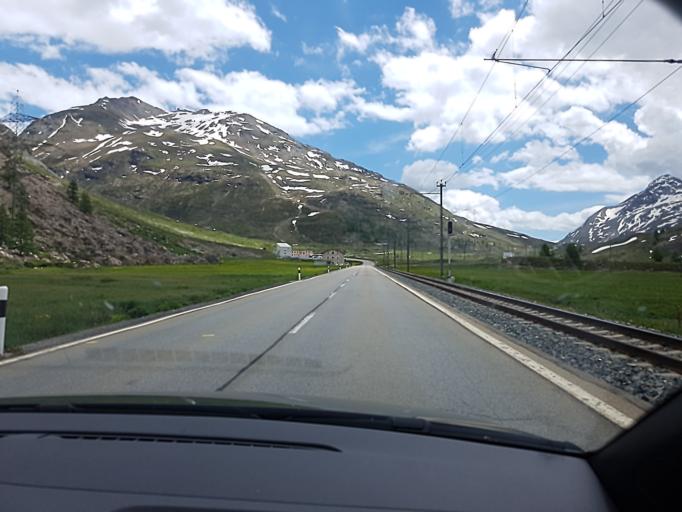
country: CH
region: Grisons
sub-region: Maloja District
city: Pontresina
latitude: 46.4397
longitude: 9.9886
